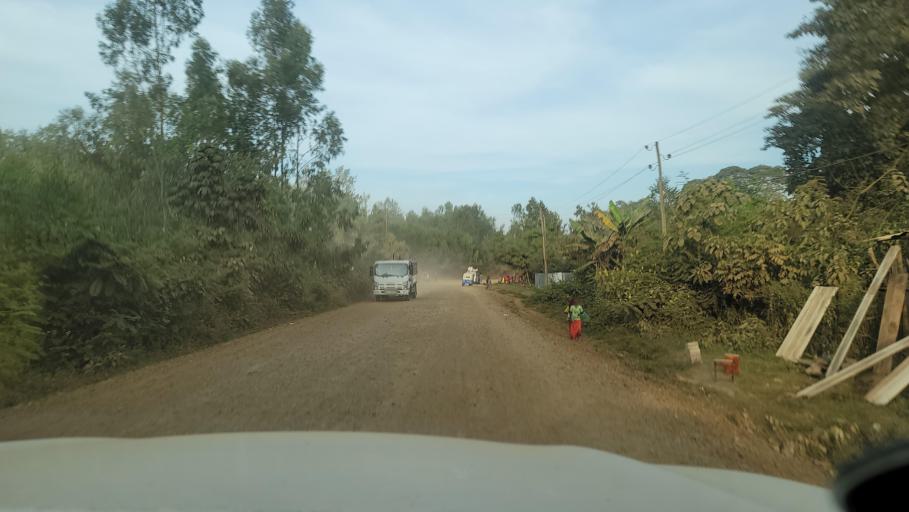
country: ET
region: Oromiya
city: Agaro
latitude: 7.8387
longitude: 36.5433
